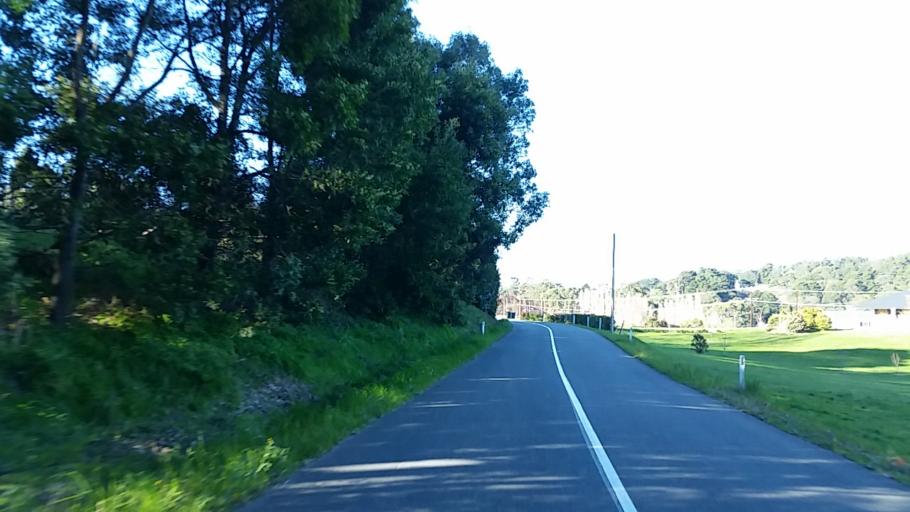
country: AU
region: South Australia
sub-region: Adelaide Hills
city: Adelaide Hills
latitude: -34.9474
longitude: 138.7226
